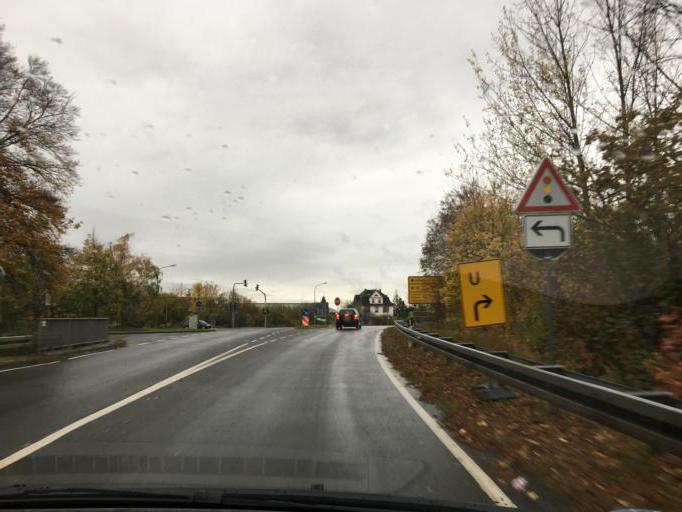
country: DE
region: North Rhine-Westphalia
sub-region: Regierungsbezirk Koln
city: Vettweiss
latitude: 50.6752
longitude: 6.5707
